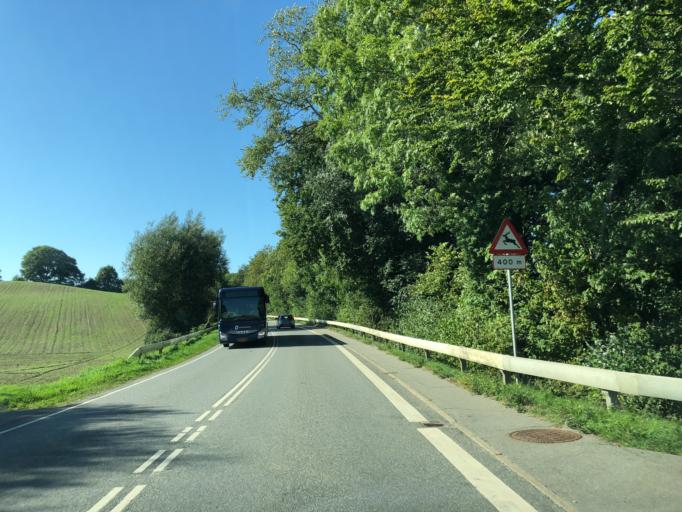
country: DK
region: South Denmark
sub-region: Aabenraa Kommune
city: Aabenraa
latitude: 55.0159
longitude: 9.4698
